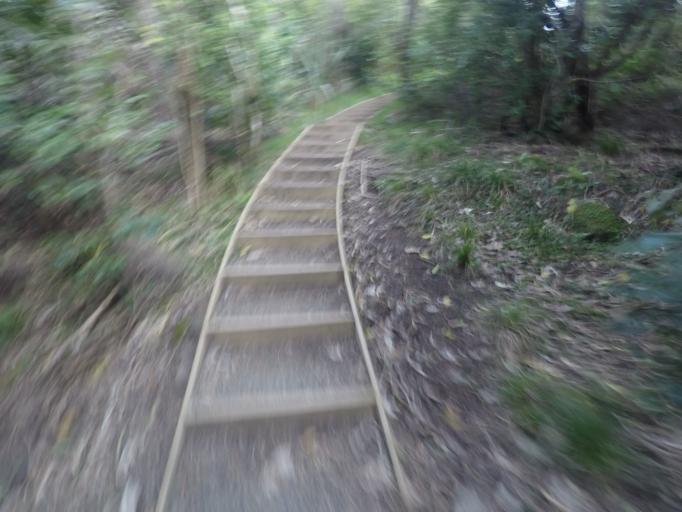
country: NZ
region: Auckland
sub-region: Auckland
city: Muriwai Beach
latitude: -36.9762
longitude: 174.4730
